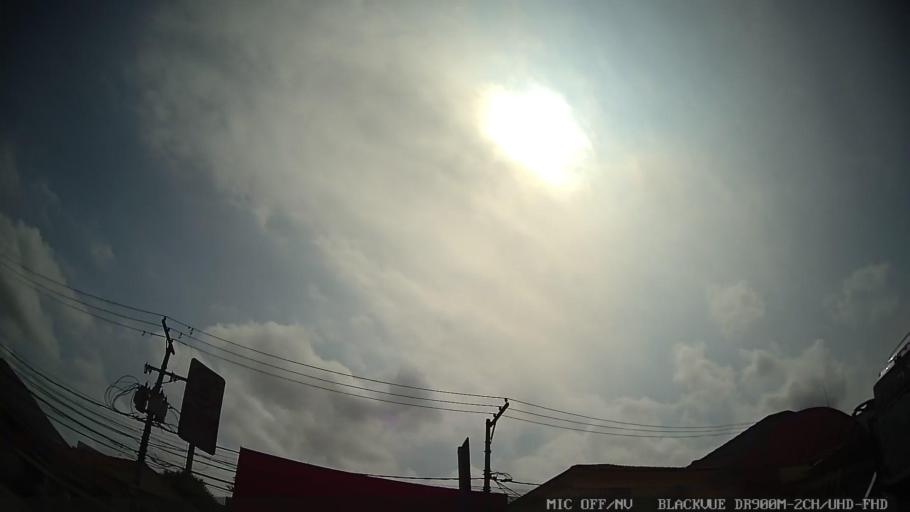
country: BR
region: Sao Paulo
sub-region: Taboao Da Serra
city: Taboao da Serra
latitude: -23.6557
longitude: -46.7077
